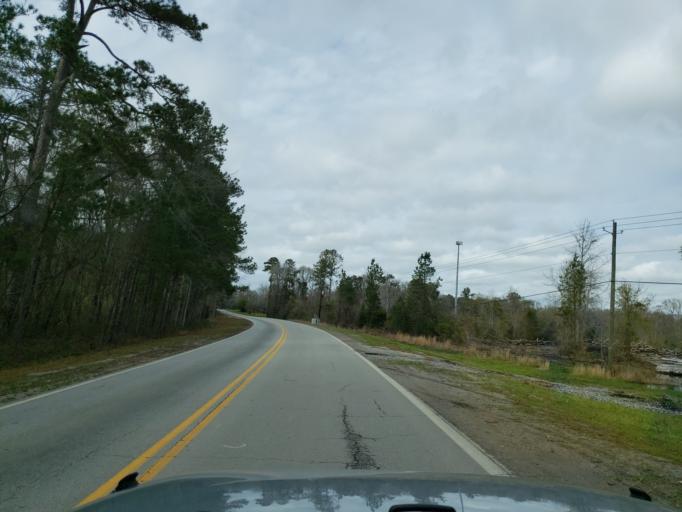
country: US
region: Georgia
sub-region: Chatham County
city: Georgetown
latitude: 32.0365
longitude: -81.2735
